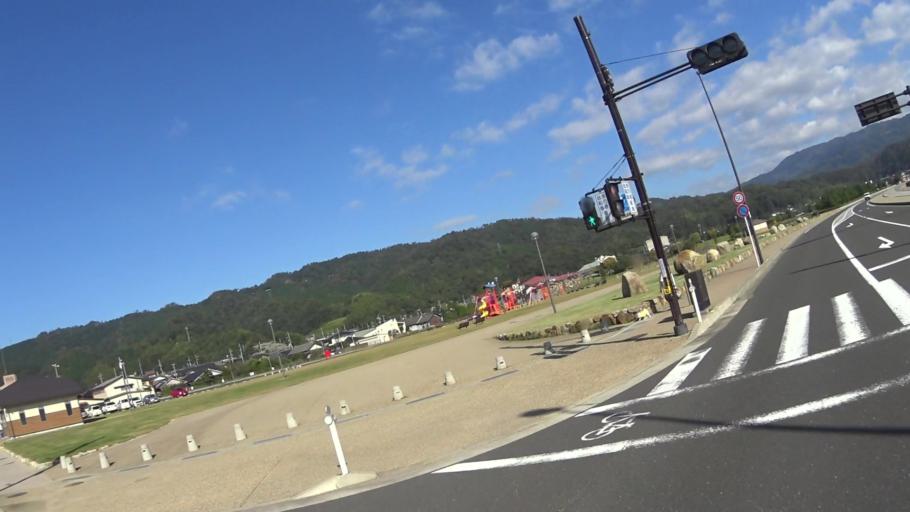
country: JP
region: Kyoto
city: Miyazu
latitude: 35.5645
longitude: 135.1553
